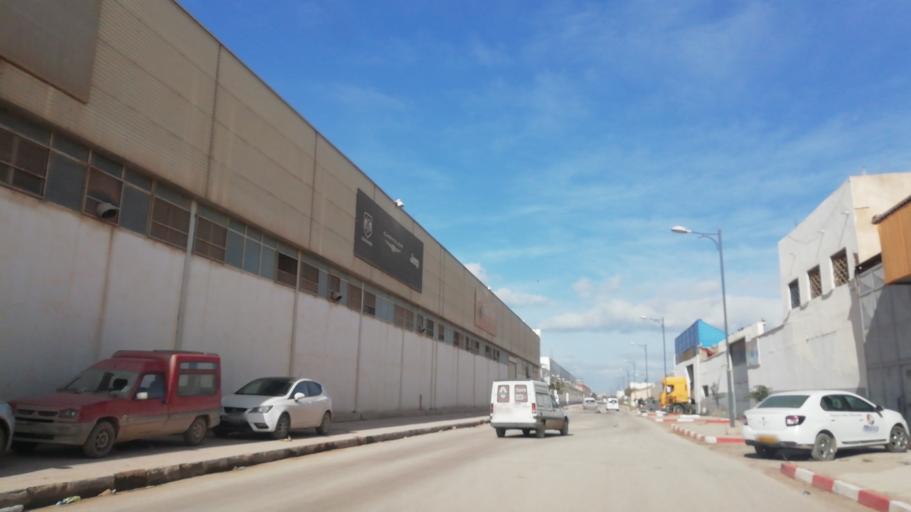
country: DZ
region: Oran
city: Es Senia
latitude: 35.6467
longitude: -0.5892
